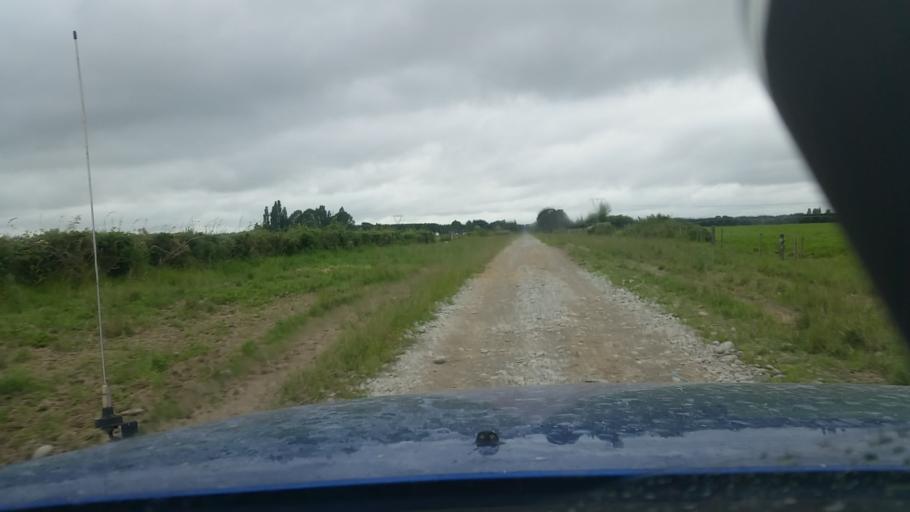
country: NZ
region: Canterbury
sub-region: Ashburton District
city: Ashburton
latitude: -43.8437
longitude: 171.6803
